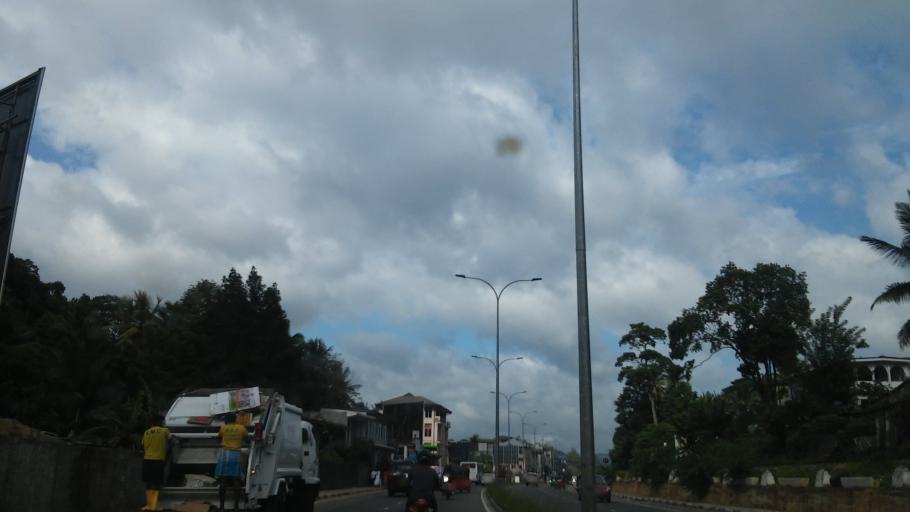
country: LK
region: Central
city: Kandy
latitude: 7.2764
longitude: 80.6160
